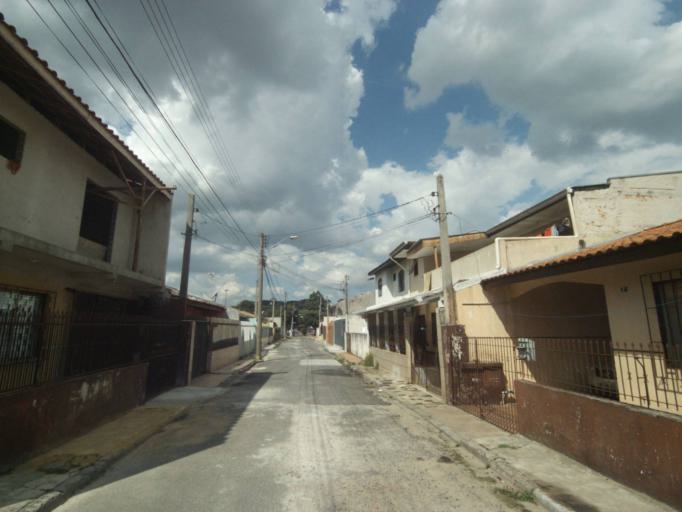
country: BR
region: Parana
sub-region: Sao Jose Dos Pinhais
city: Sao Jose dos Pinhais
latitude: -25.5304
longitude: -49.2606
